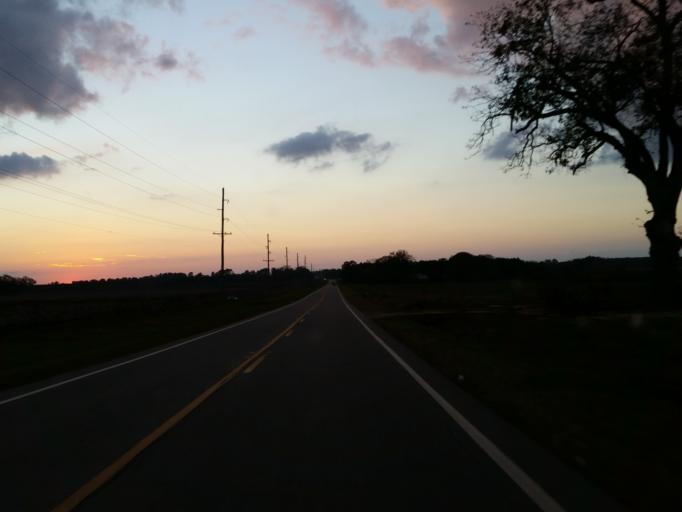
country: US
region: Georgia
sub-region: Dooly County
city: Vienna
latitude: 32.1235
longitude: -83.7185
